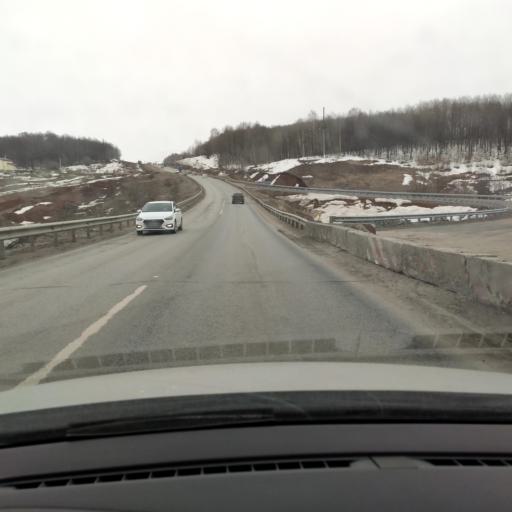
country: RU
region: Tatarstan
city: Vysokaya Gora
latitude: 55.8069
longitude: 49.4079
